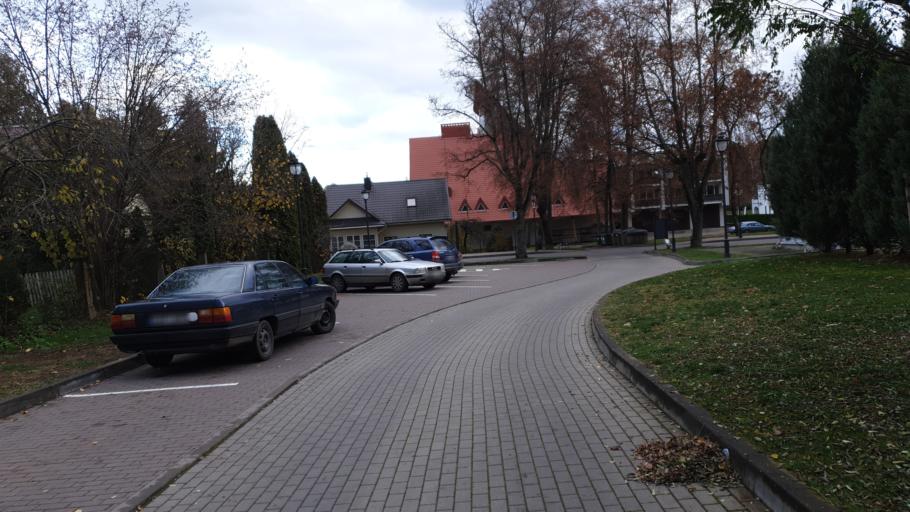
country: LT
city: Birstonas
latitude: 54.6023
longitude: 24.0336
